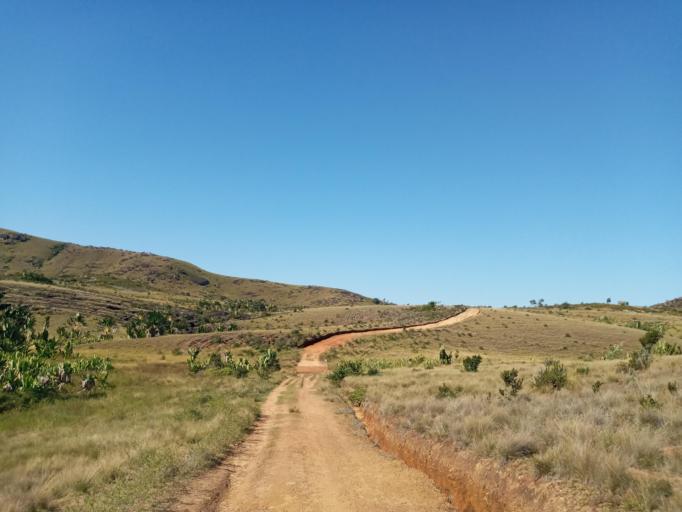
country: MG
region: Anosy
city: Fort Dauphin
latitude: -24.9094
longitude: 47.0766
